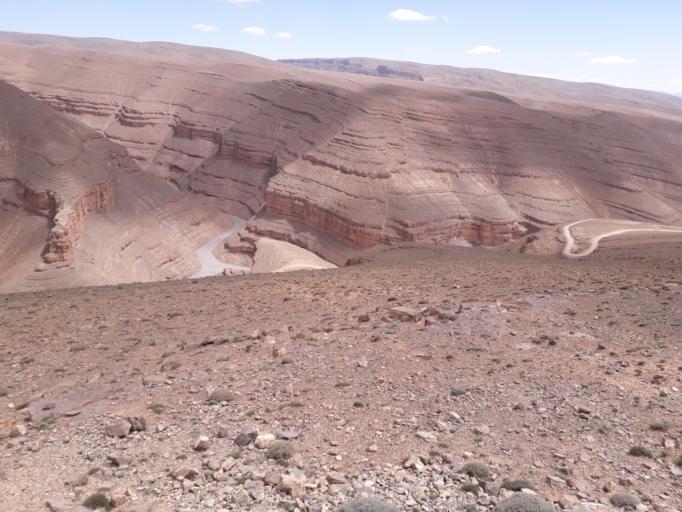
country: MA
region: Souss-Massa-Draa
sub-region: Ouarzazate
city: Tilmi
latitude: 31.8622
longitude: -5.7186
